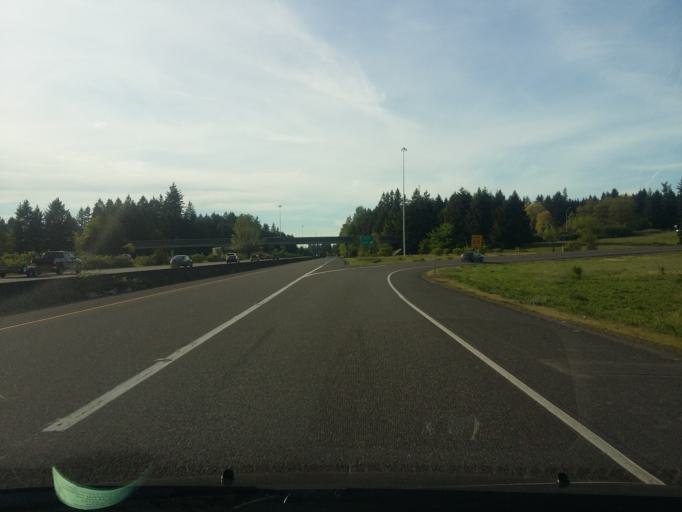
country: US
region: Washington
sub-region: Clark County
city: Orchards
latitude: 45.6572
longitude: -122.5706
